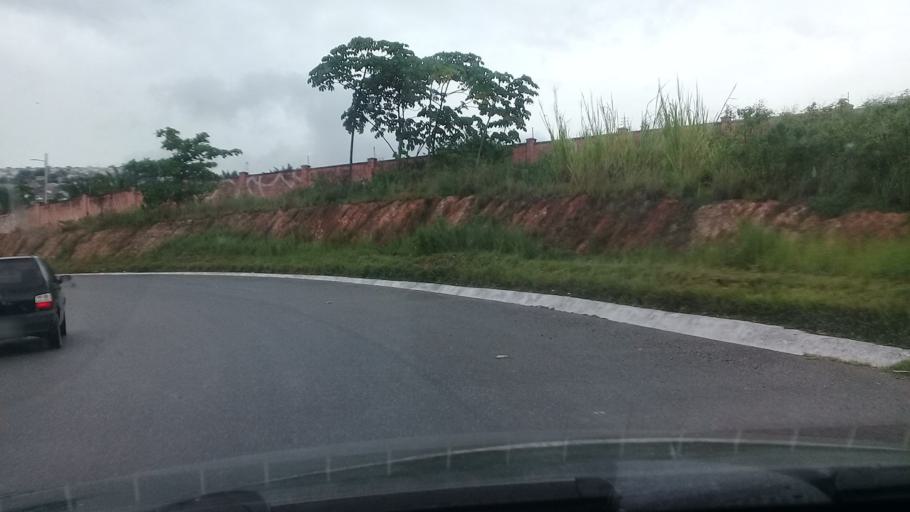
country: BR
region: Pernambuco
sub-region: Jaboatao Dos Guararapes
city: Jaboatao dos Guararapes
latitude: -8.0646
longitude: -34.9909
